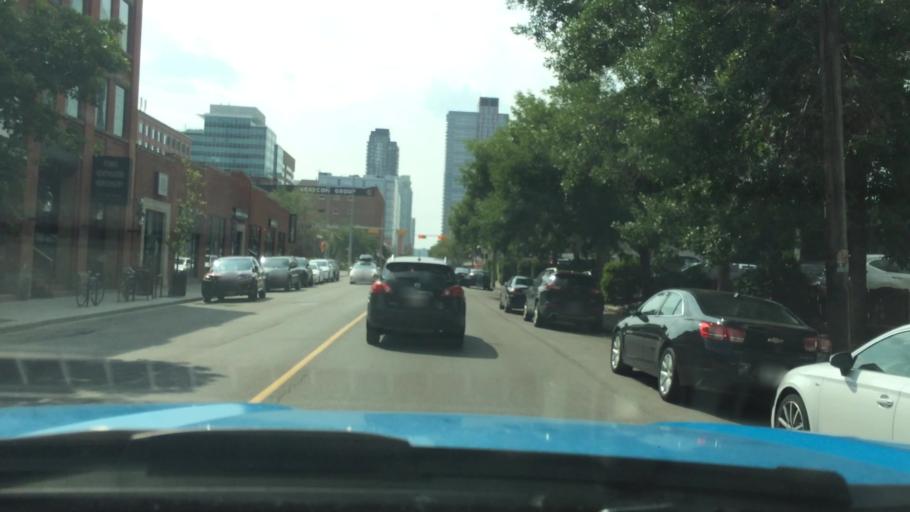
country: CA
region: Alberta
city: Calgary
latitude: 51.0434
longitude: -114.0664
